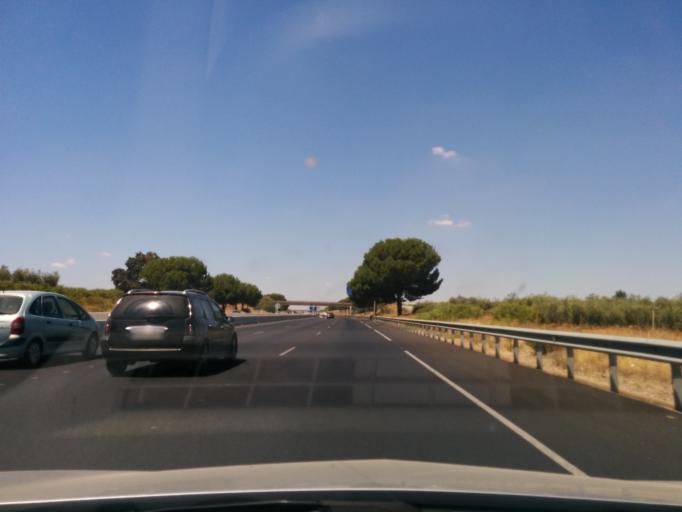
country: ES
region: Andalusia
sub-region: Provincia de Sevilla
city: Umbrete
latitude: 37.3584
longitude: -6.1582
